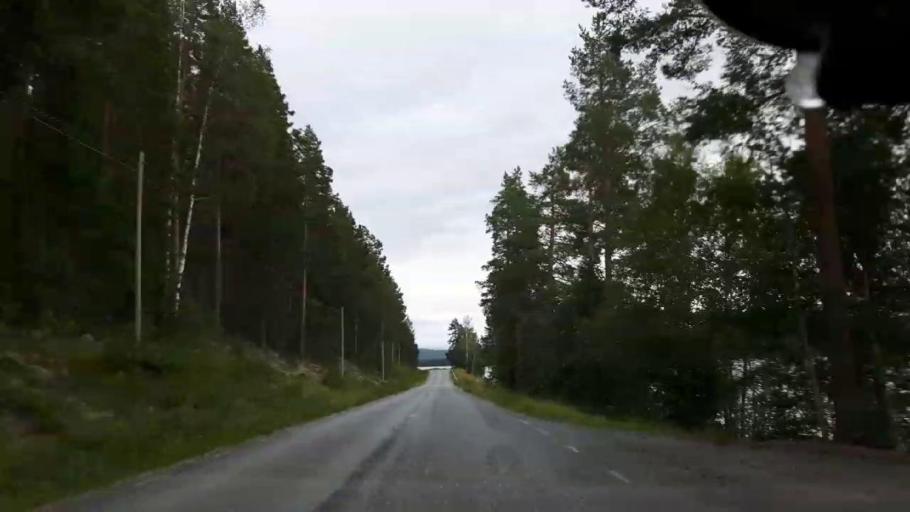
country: SE
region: Jaemtland
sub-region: Braecke Kommun
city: Braecke
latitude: 62.8667
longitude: 15.6169
